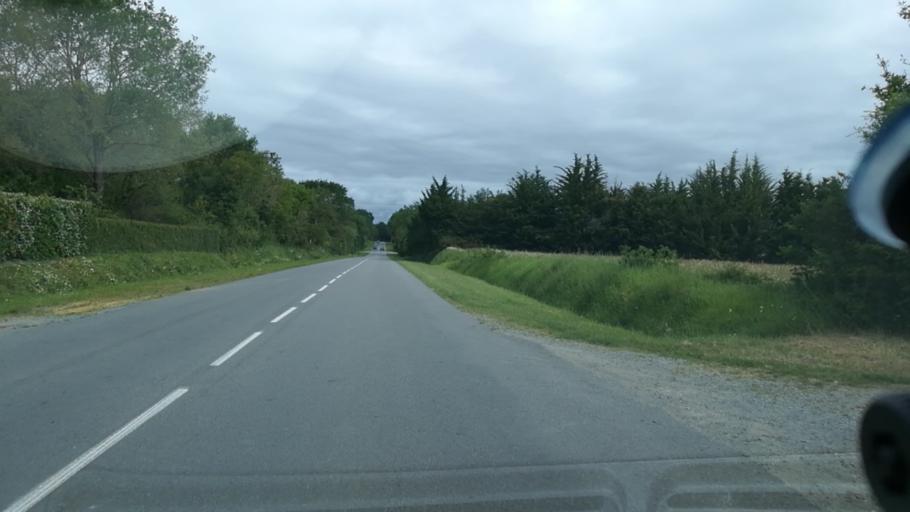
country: FR
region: Brittany
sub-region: Departement du Morbihan
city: Penestin
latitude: 47.4625
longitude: -2.4778
